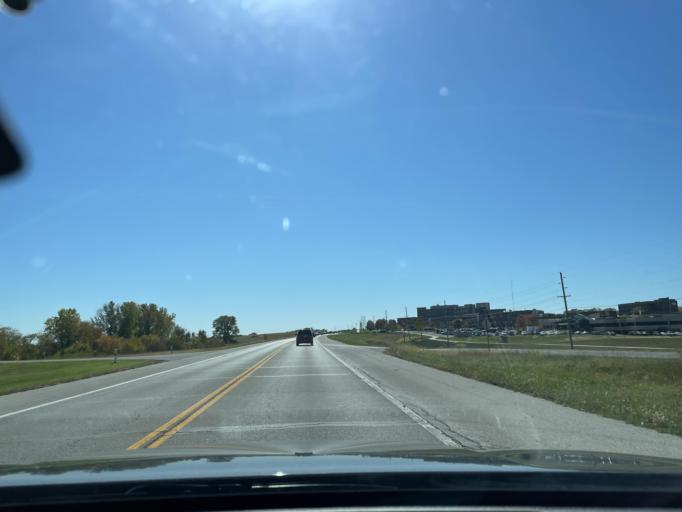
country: US
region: Missouri
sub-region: Andrew County
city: Country Club Village
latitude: 39.7784
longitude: -94.7675
